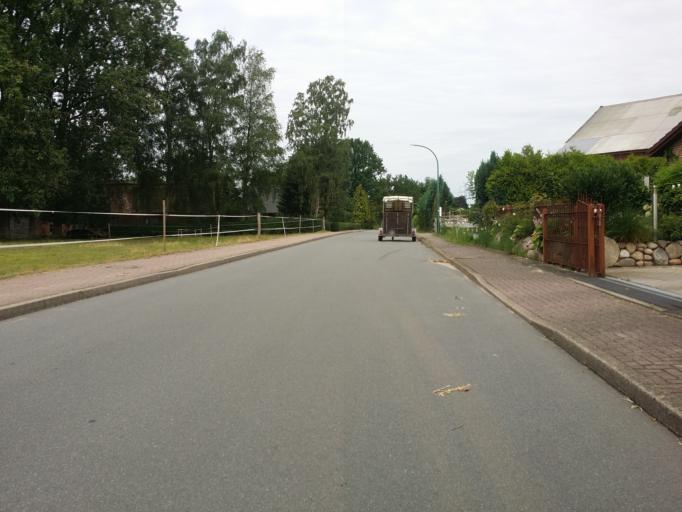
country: DE
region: Schleswig-Holstein
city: Oldendorf
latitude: 53.9582
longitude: 9.4505
